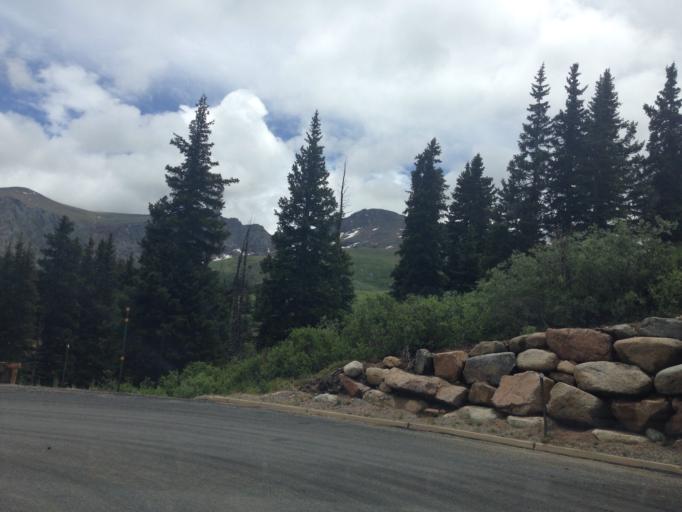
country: US
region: Colorado
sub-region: Clear Creek County
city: Georgetown
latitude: 39.5989
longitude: -105.7081
